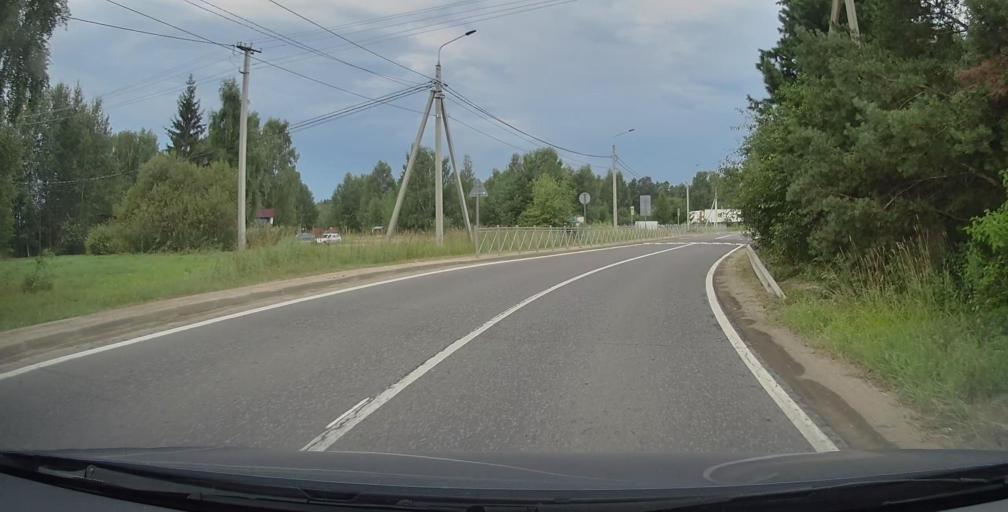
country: RU
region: Jaroslavl
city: Myshkin
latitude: 57.7985
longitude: 38.5064
